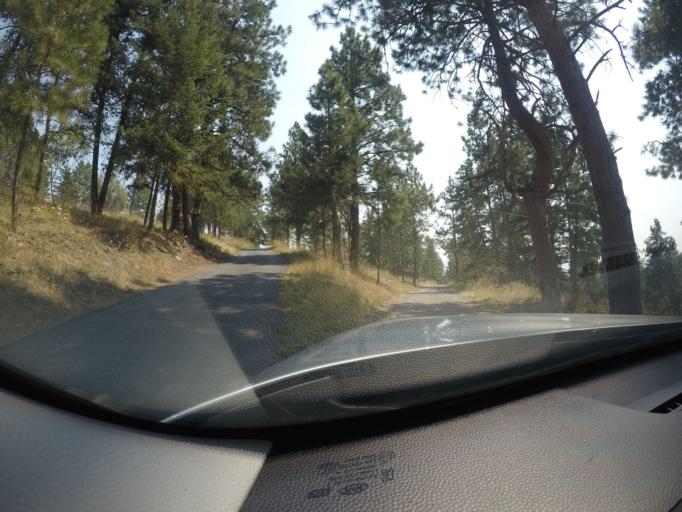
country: US
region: Montana
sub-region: Lake County
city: Polson
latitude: 47.7582
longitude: -114.1425
